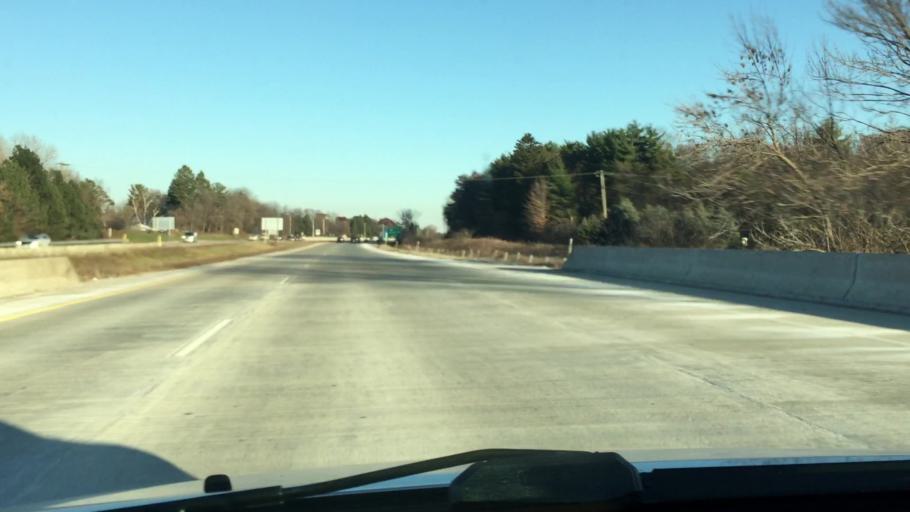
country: US
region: Wisconsin
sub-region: Waukesha County
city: Okauchee Lake
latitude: 43.1081
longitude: -88.4533
